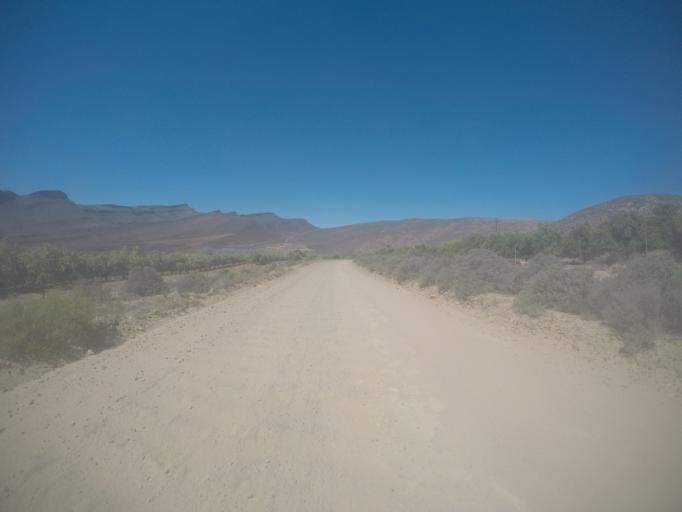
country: ZA
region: Western Cape
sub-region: West Coast District Municipality
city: Clanwilliam
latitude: -32.5586
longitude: 19.3615
